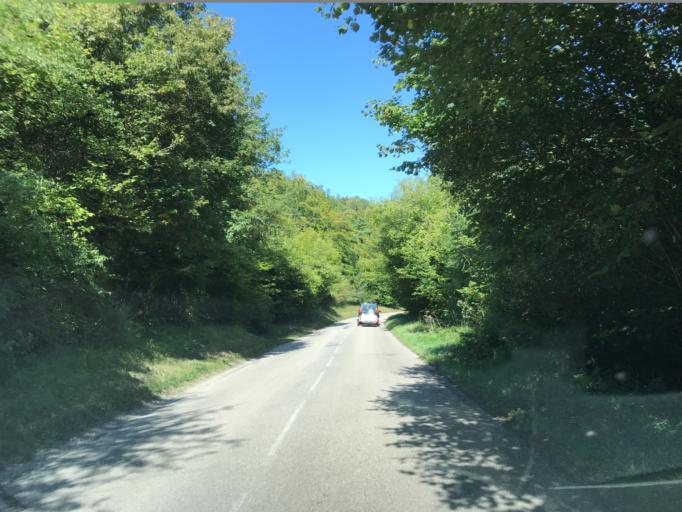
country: FR
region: Haute-Normandie
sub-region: Departement de l'Eure
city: Heudreville-sur-Eure
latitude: 49.1060
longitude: 1.2064
